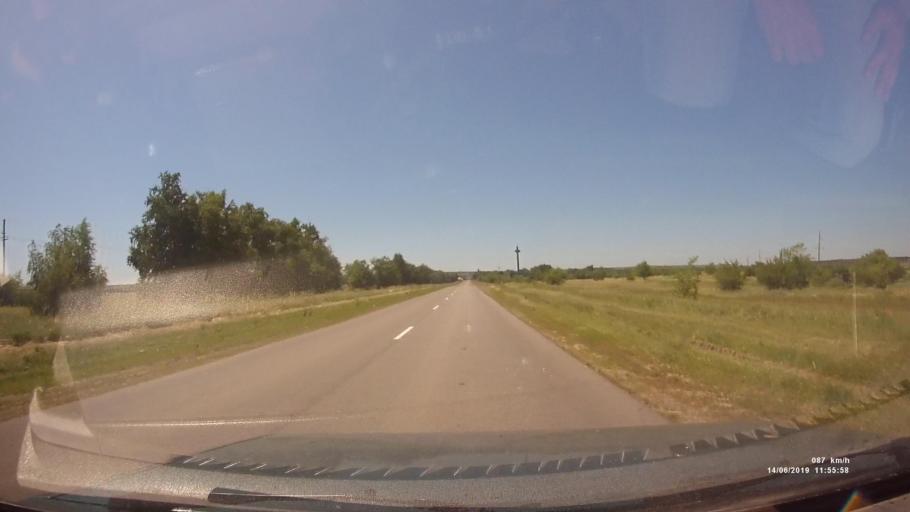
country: RU
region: Rostov
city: Kazanskaya
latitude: 49.8062
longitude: 41.1681
